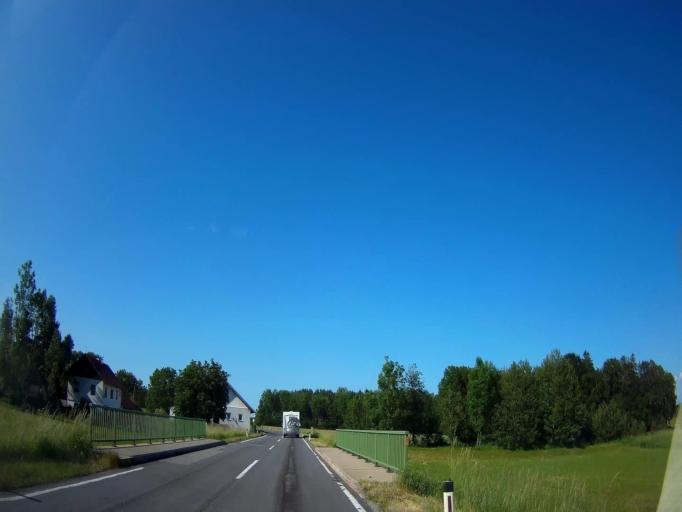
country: AT
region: Upper Austria
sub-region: Politischer Bezirk Braunau am Inn
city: Braunau am Inn
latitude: 48.1599
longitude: 13.0479
